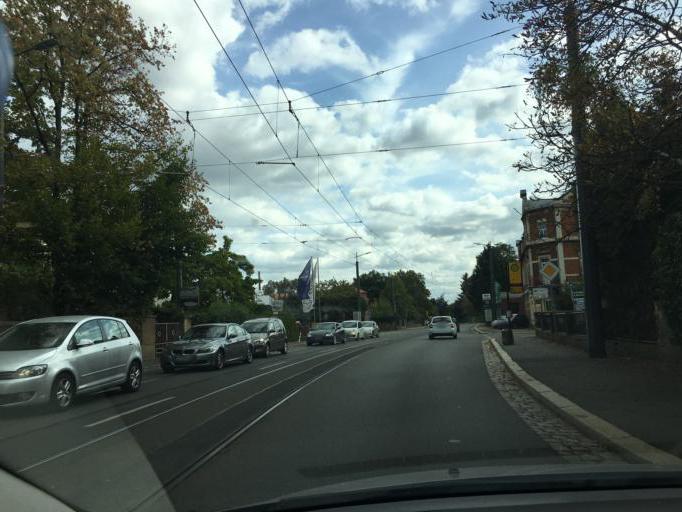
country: DE
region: Saxony
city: Radebeul
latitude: 51.1108
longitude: 13.6242
